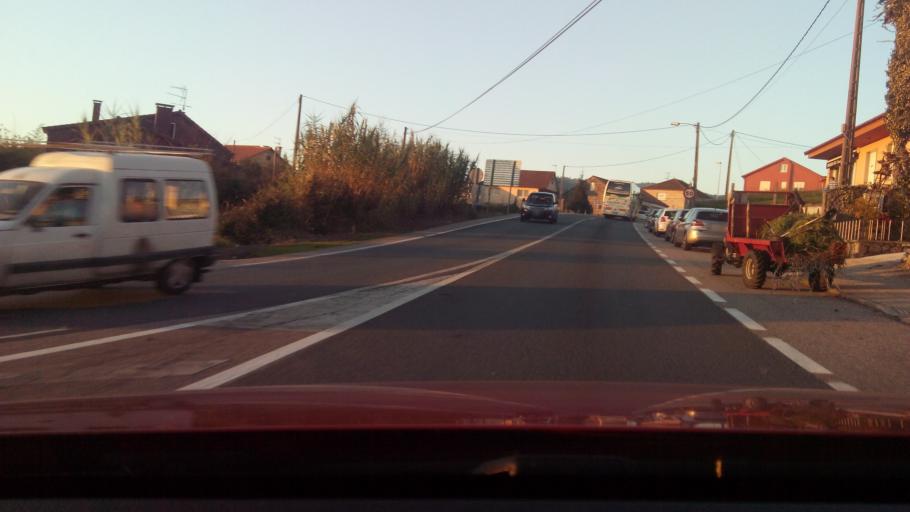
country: ES
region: Galicia
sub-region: Provincia de Pontevedra
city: Gondomar
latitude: 42.1375
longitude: -8.7315
